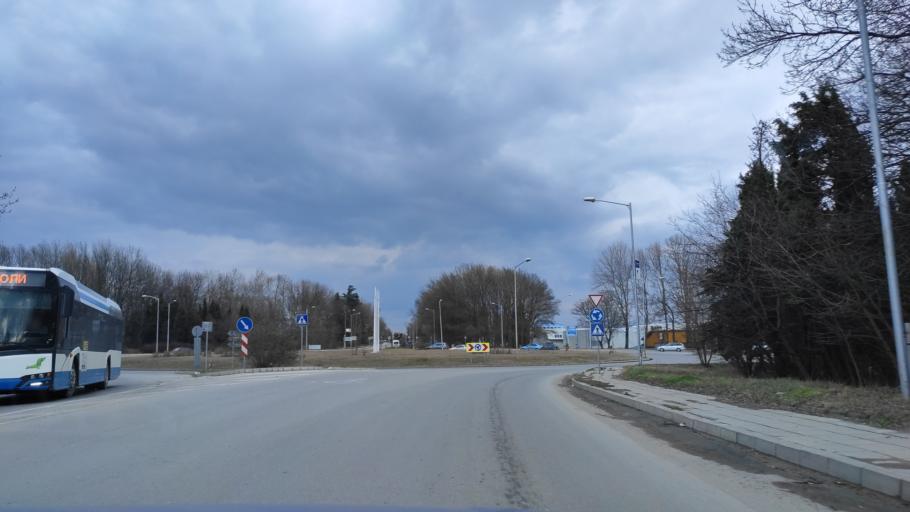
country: BG
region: Varna
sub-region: Obshtina Aksakovo
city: Aksakovo
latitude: 43.2260
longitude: 27.8579
